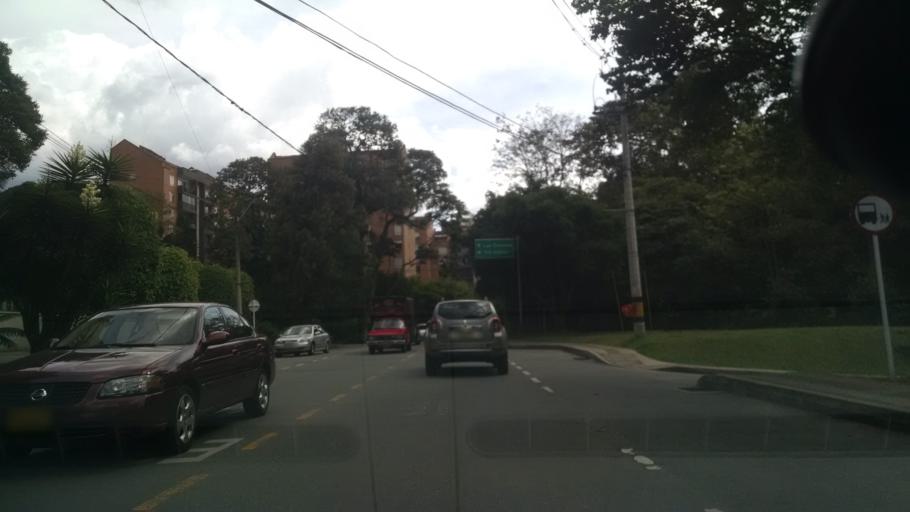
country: CO
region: Antioquia
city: Envigado
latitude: 6.2001
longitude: -75.5664
